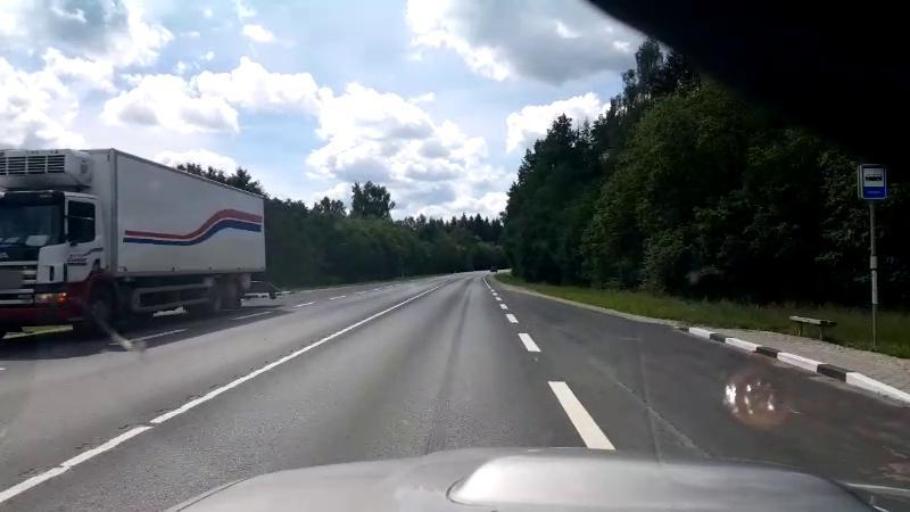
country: EE
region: Laeaene-Virumaa
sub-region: Tapa vald
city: Tapa
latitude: 59.2795
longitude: 26.0409
